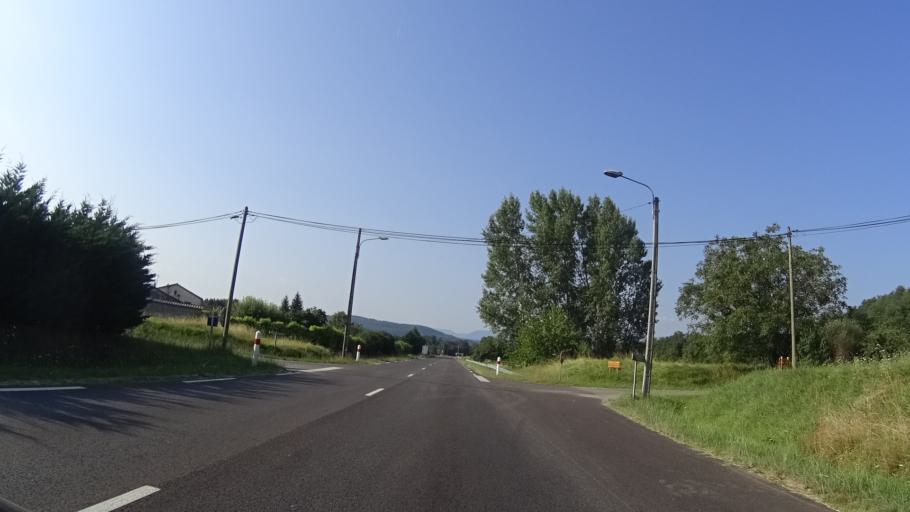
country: FR
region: Midi-Pyrenees
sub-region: Departement de l'Ariege
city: Mirepoix
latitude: 43.0327
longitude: 1.8970
